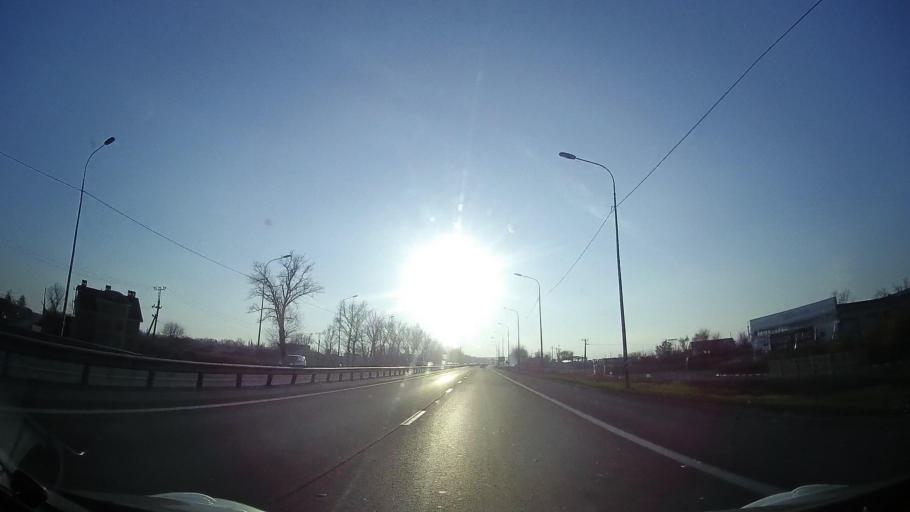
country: RU
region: Rostov
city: Bataysk
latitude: 47.1195
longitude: 39.8606
